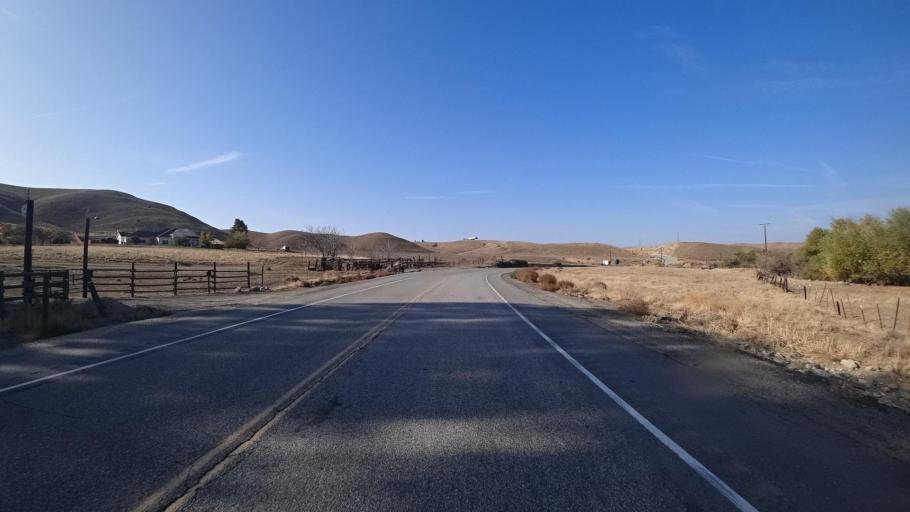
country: US
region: California
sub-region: Kern County
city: Oildale
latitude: 35.5273
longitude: -118.9692
